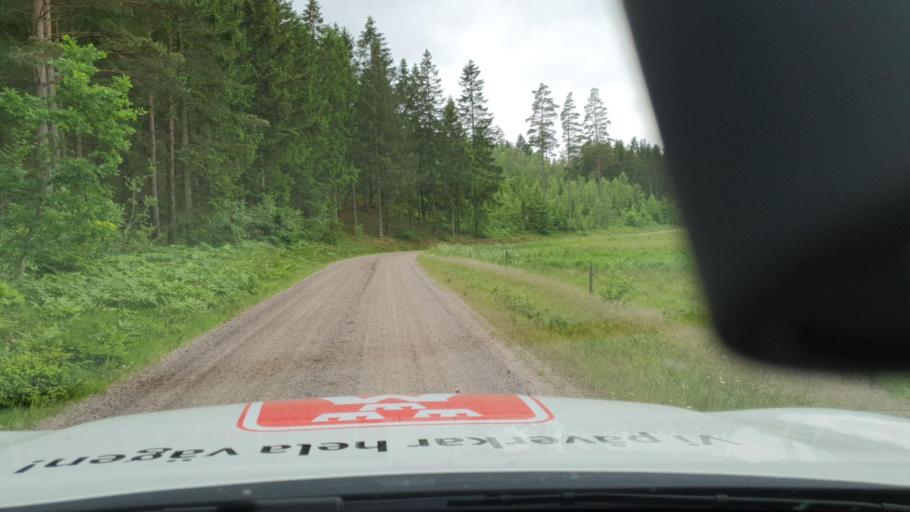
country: SE
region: Vaestra Goetaland
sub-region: Hjo Kommun
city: Hjo
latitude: 58.3477
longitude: 14.3212
